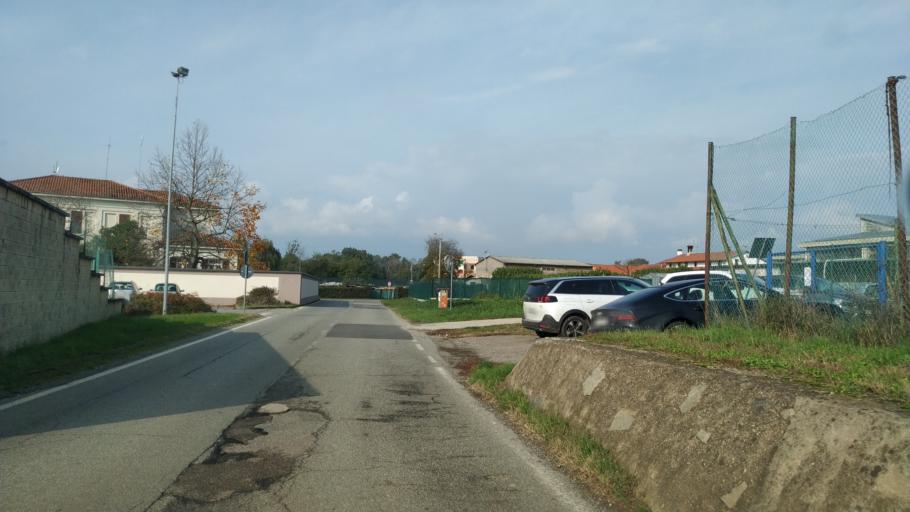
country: IT
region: Piedmont
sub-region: Provincia di Biella
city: Vergnasco
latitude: 45.4807
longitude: 8.0749
